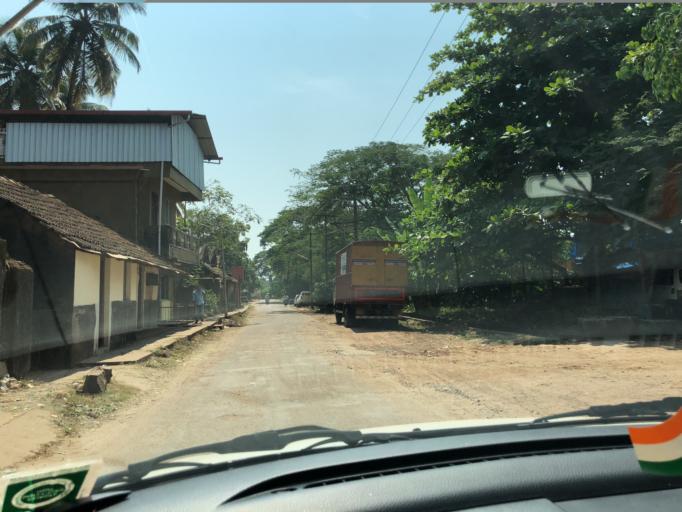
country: IN
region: Karnataka
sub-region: Dakshina Kannada
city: Ullal
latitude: 12.8568
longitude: 74.8347
